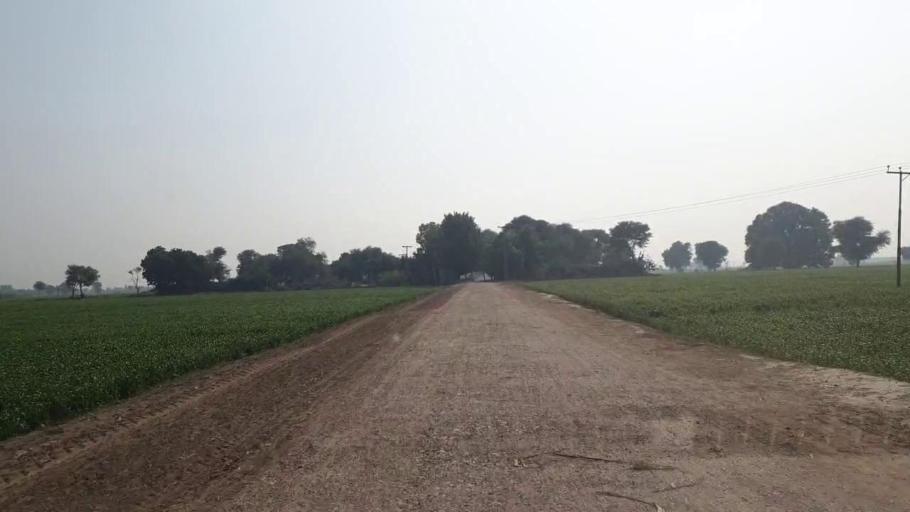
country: PK
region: Sindh
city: Hala
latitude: 25.8284
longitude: 68.4589
